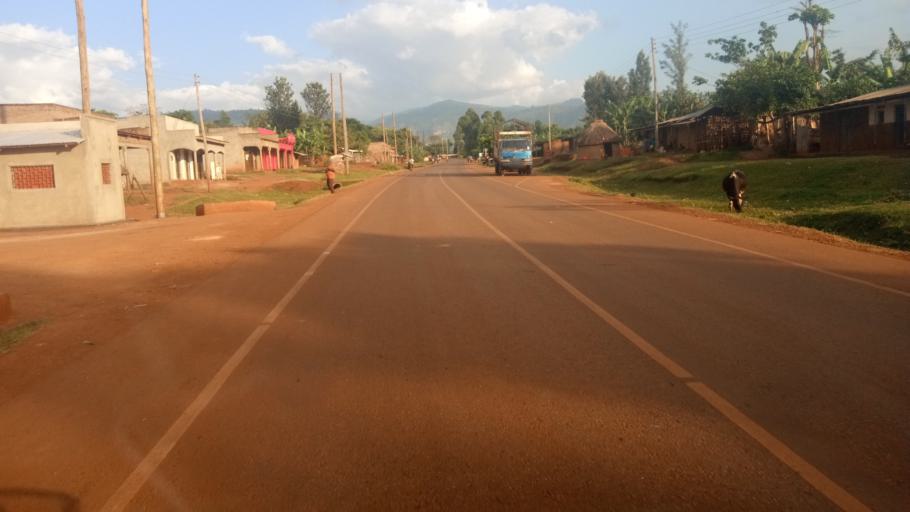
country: UG
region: Eastern Region
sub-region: Sironko District
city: Sironko
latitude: 1.3212
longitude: 34.3365
